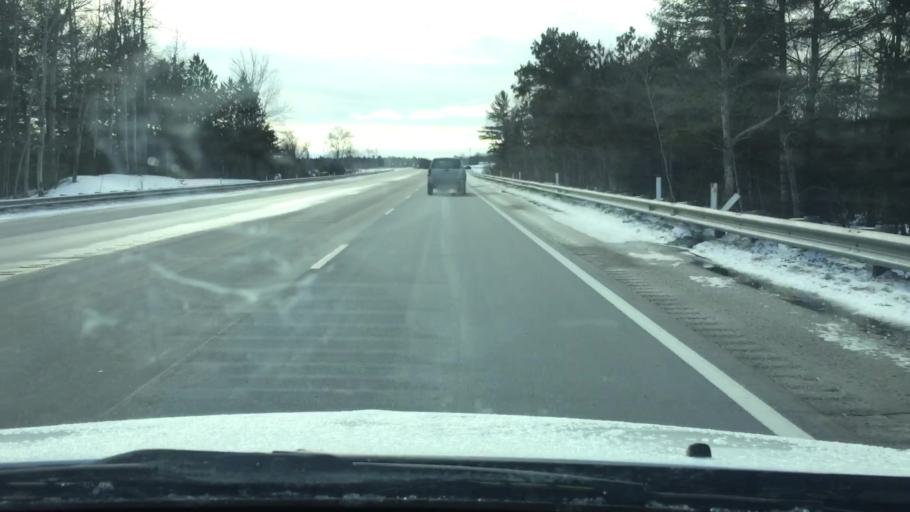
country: US
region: Michigan
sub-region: Kalkaska County
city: Kalkaska
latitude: 44.6769
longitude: -85.2327
